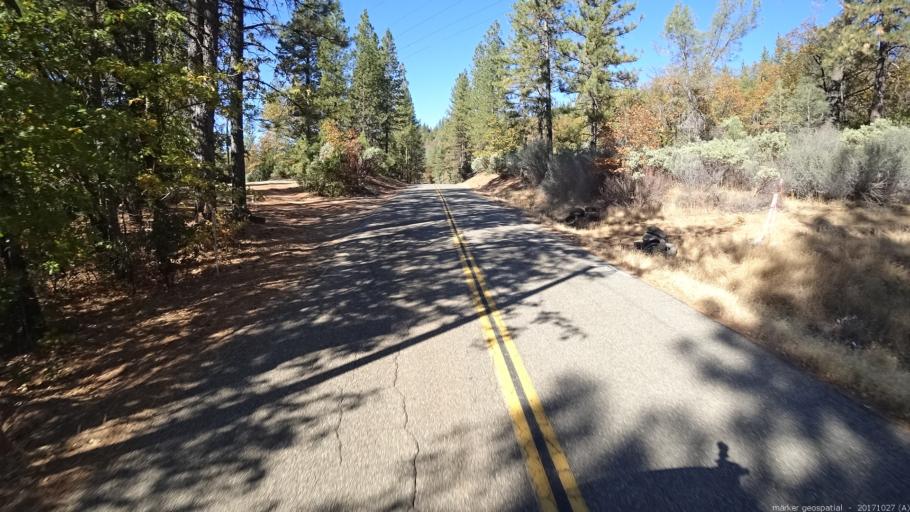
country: US
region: California
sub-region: Shasta County
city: Shingletown
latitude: 40.6836
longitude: -121.8892
